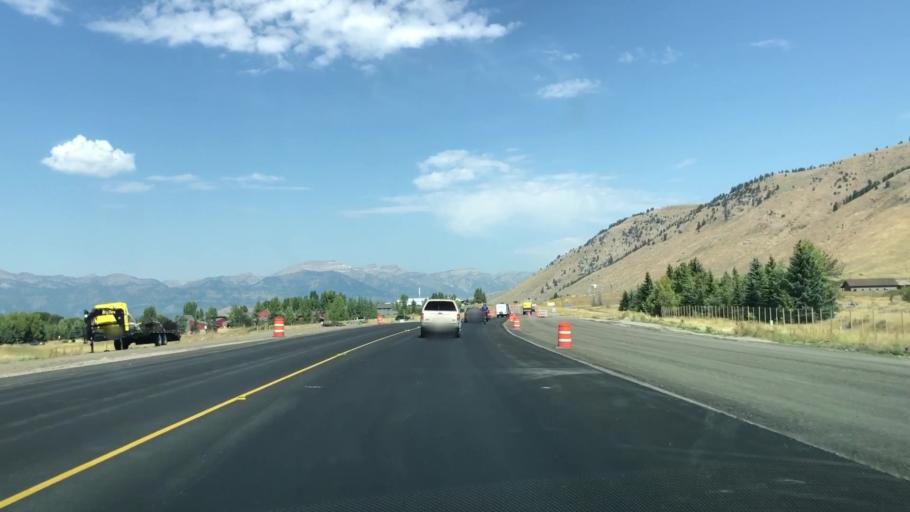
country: US
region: Wyoming
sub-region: Teton County
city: South Park
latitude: 43.4131
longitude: -110.7725
